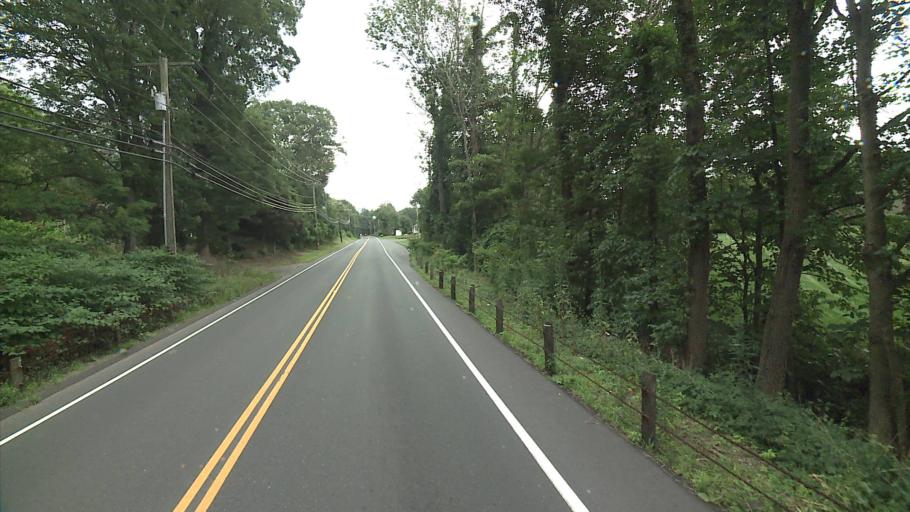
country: US
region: Connecticut
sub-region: New Haven County
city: Southbury
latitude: 41.4731
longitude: -73.1872
